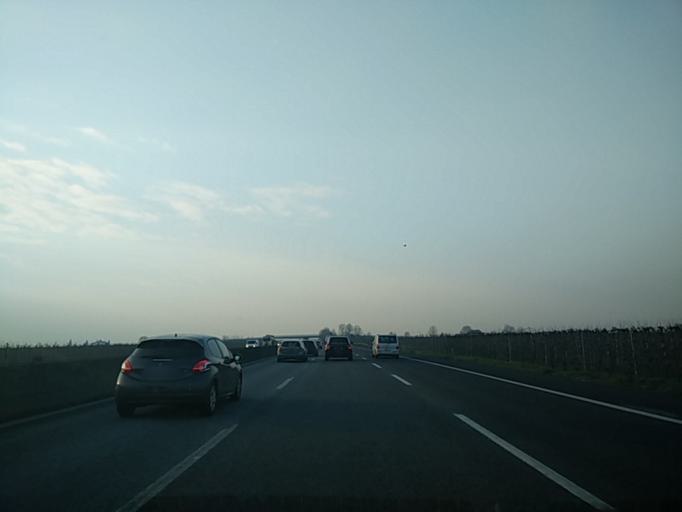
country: IT
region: Emilia-Romagna
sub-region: Provincia di Bologna
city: Mordano
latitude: 44.3680
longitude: 11.7772
